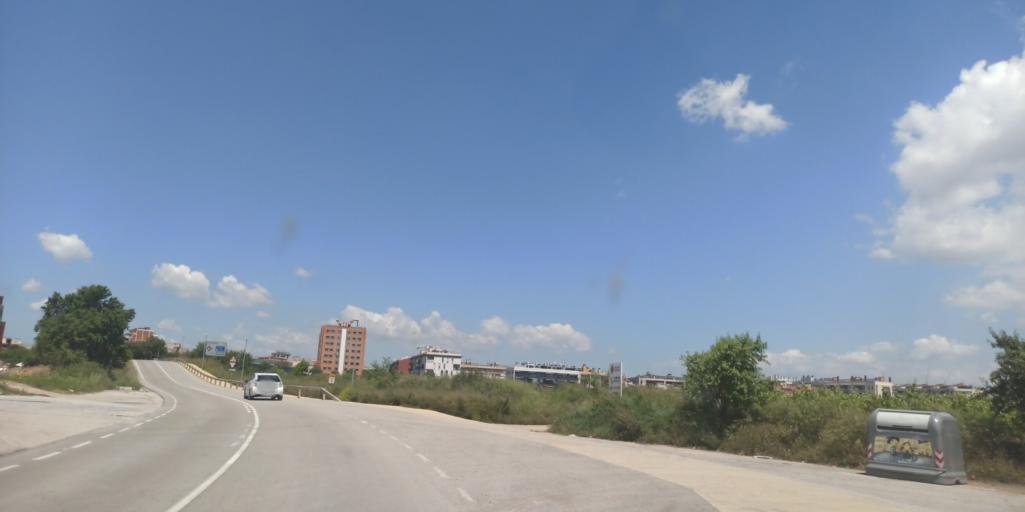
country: ES
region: Catalonia
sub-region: Provincia de Barcelona
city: Vilafranca del Penedes
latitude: 41.3321
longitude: 1.6980
